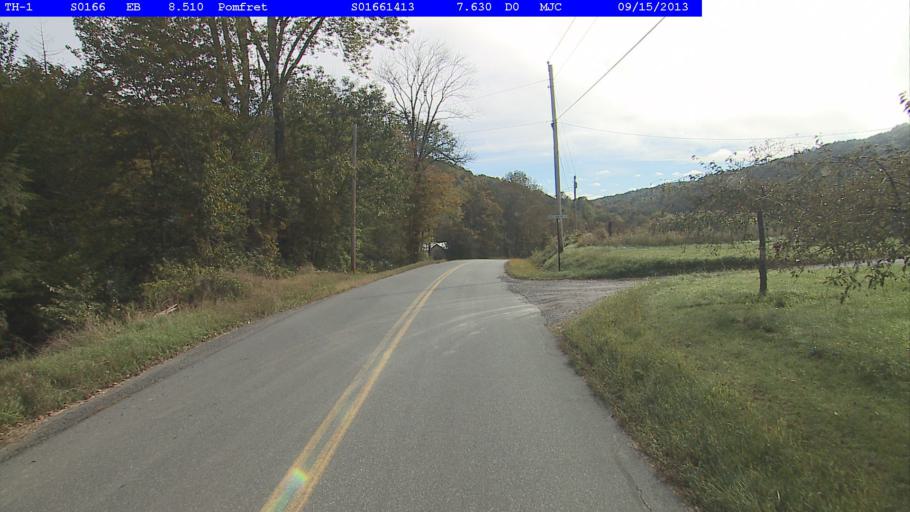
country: US
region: Vermont
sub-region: Windsor County
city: Woodstock
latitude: 43.7256
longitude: -72.4706
